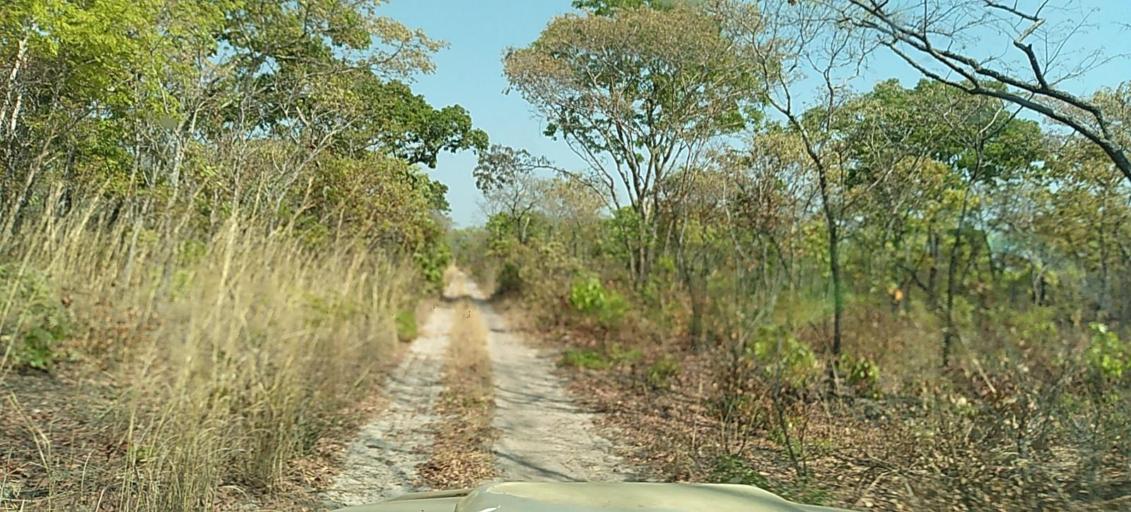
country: ZM
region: North-Western
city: Kalengwa
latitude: -13.3308
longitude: 24.8419
